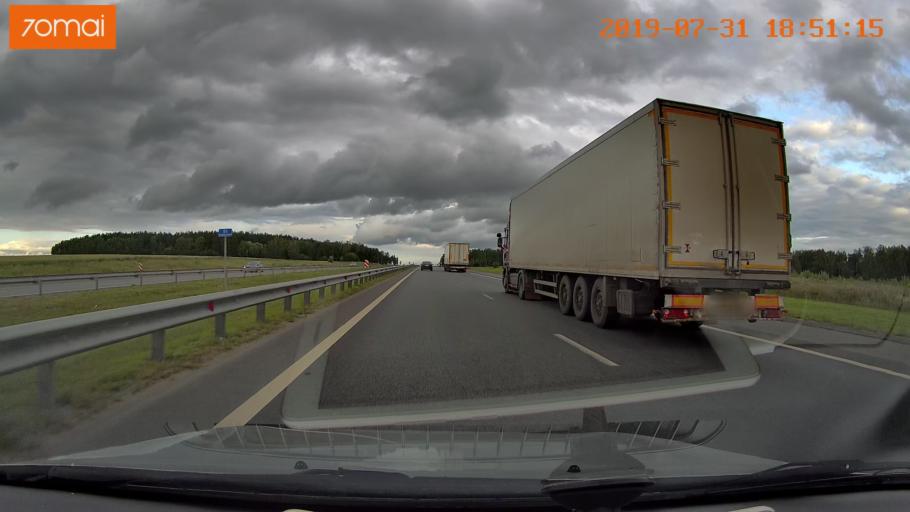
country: RU
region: Moskovskaya
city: Troitskoye
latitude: 55.2228
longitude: 38.6021
